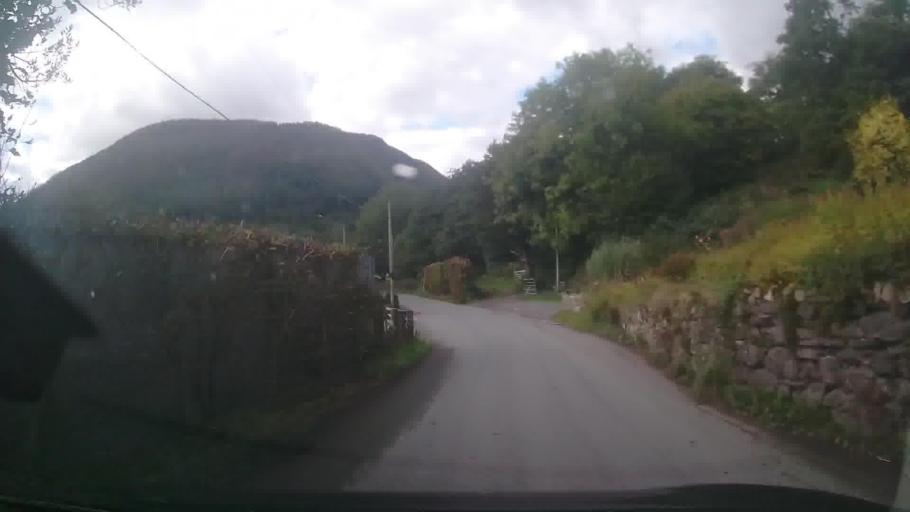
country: GB
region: Wales
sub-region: Gwynedd
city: Corris
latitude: 52.7227
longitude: -3.6869
